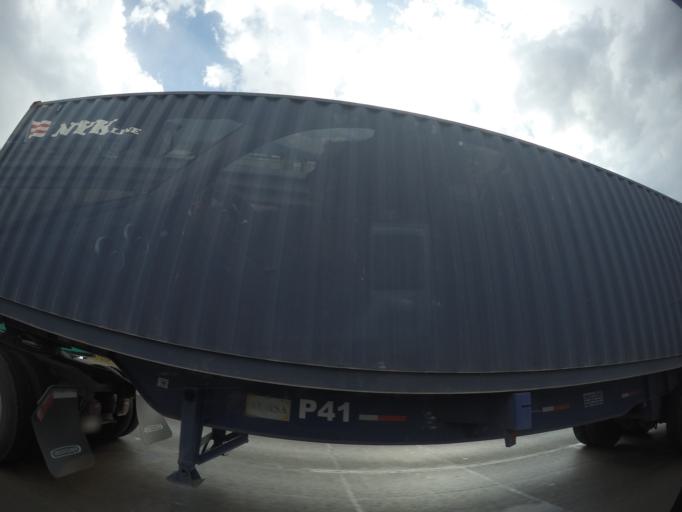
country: MX
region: Mexico
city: San Francisco Soyaniquilpan
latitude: 19.9933
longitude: -99.4723
